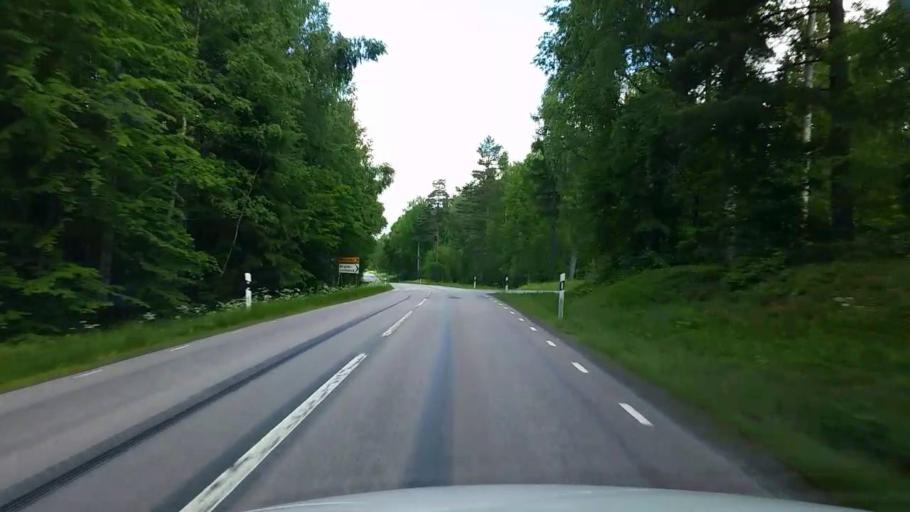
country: SE
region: Vaestmanland
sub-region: Kopings Kommun
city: Kolsva
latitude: 59.6728
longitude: 15.7701
